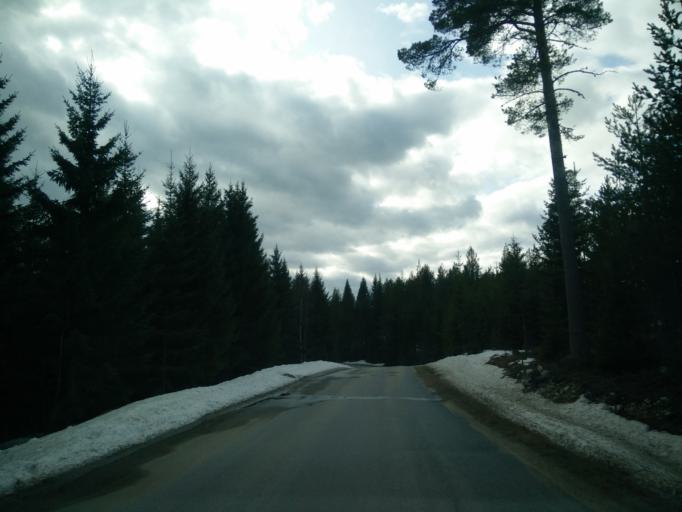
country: SE
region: Vaesternorrland
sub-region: Haernoesands Kommun
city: Haernoesand
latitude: 62.7129
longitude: 18.0489
